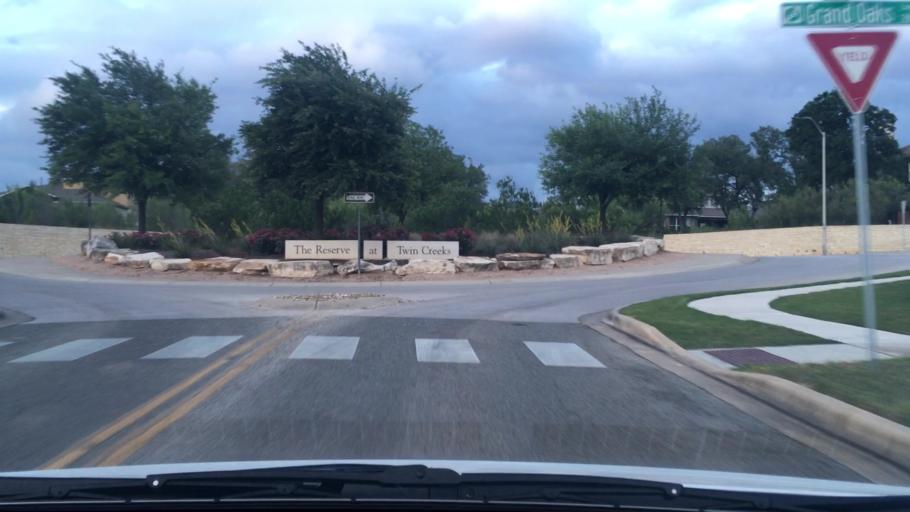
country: US
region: Texas
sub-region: Williamson County
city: Anderson Mill
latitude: 30.4540
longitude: -97.8587
